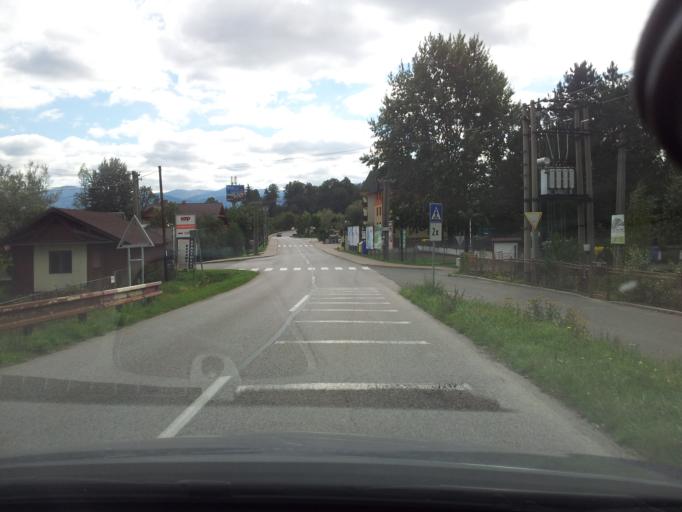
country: SK
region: Zilinsky
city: Ruzomberok
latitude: 49.1007
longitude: 19.4343
